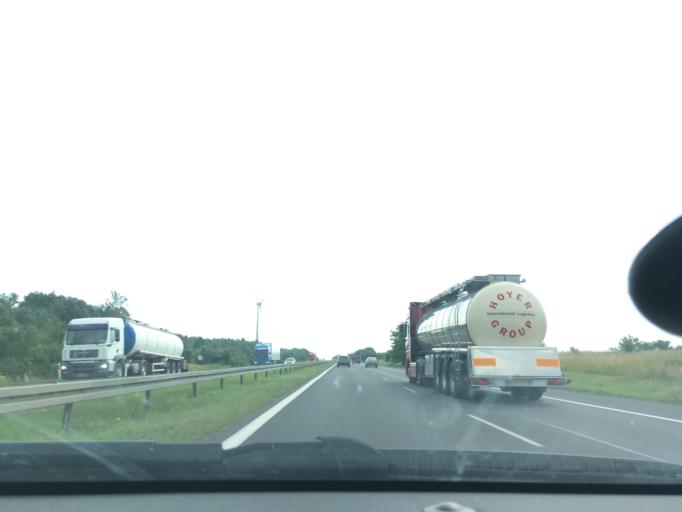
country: PL
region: Lodz Voivodeship
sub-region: Powiat radomszczanski
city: Gomunice
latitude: 51.1496
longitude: 19.4368
